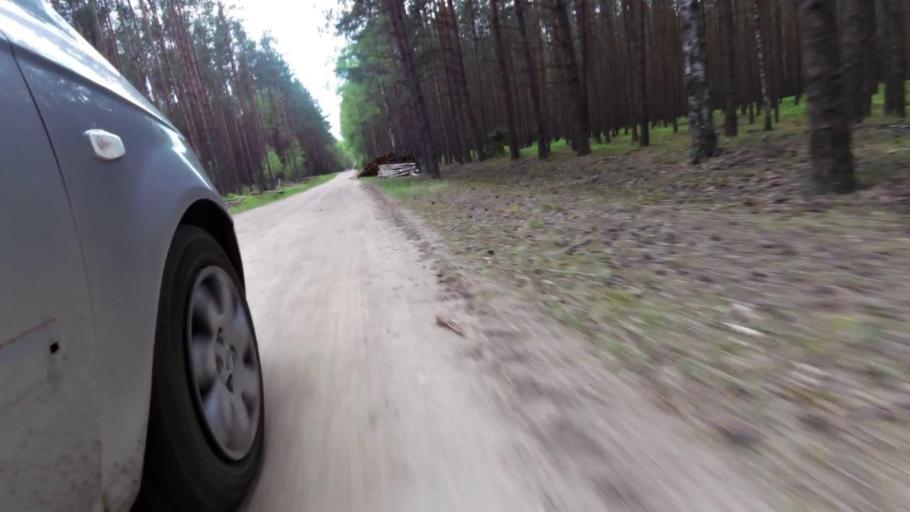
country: PL
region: West Pomeranian Voivodeship
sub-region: Powiat walecki
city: Walcz
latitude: 53.2711
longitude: 16.3829
